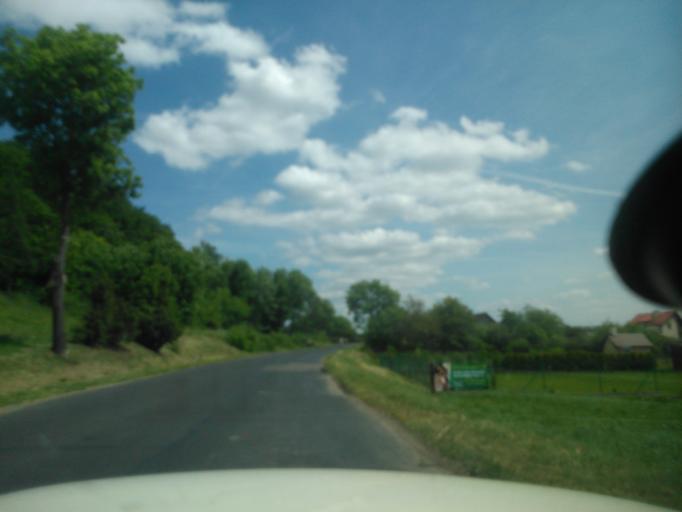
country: PL
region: Kujawsko-Pomorskie
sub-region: Powiat golubsko-dobrzynski
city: Golub-Dobrzyn
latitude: 53.1091
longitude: 19.0356
